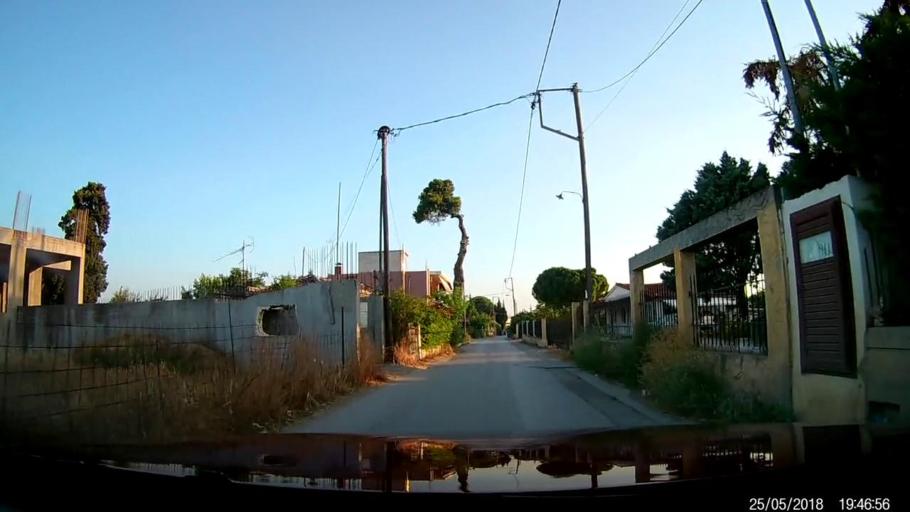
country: GR
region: Central Greece
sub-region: Nomos Evvoias
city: Ayios Nikolaos
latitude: 38.4247
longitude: 23.6403
